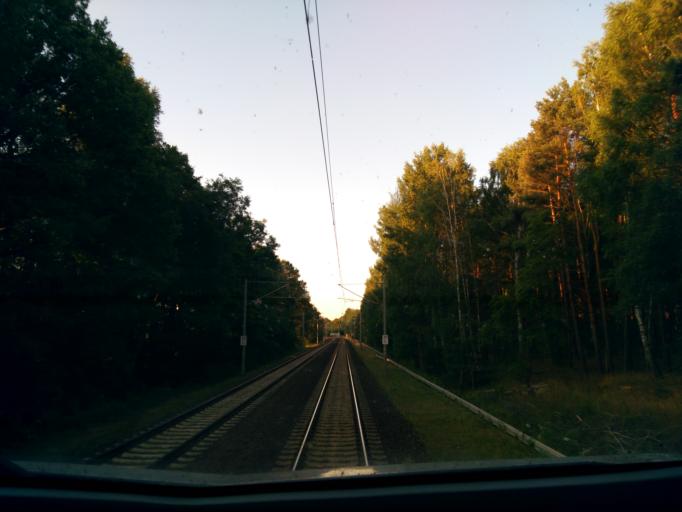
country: DE
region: Brandenburg
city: Schwerin
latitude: 52.1990
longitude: 13.6236
